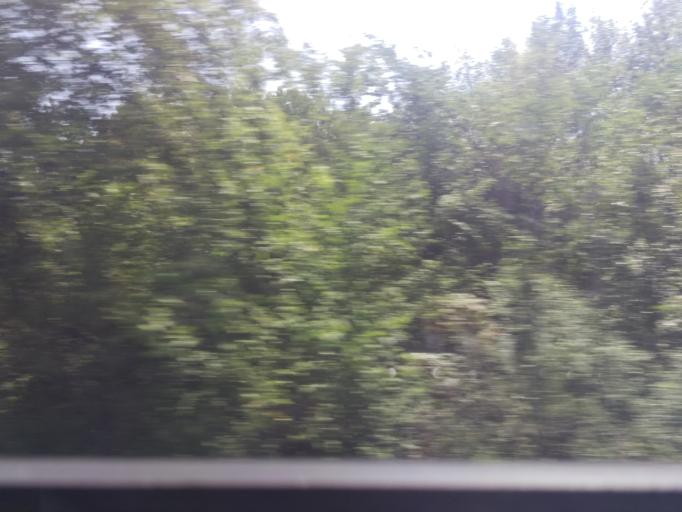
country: CA
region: Ontario
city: Belleville
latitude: 44.1873
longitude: -77.3444
